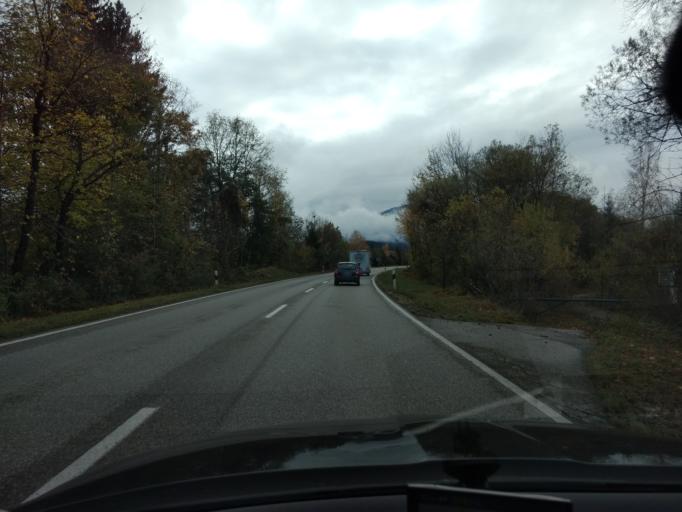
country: DE
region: Bavaria
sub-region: Upper Bavaria
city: Lenggries
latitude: 47.6657
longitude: 11.5823
